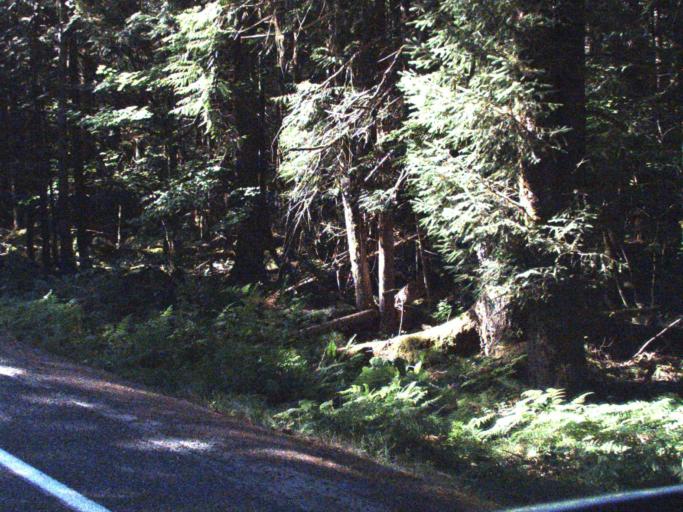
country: US
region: Washington
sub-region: King County
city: Riverbend
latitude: 47.1345
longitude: -121.6216
